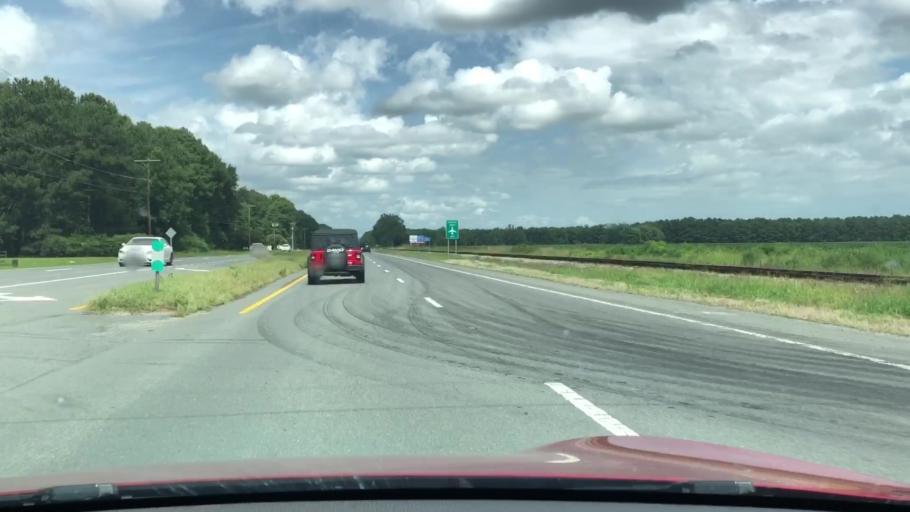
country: US
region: Virginia
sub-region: Accomack County
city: Onancock
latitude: 37.6335
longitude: -75.7533
